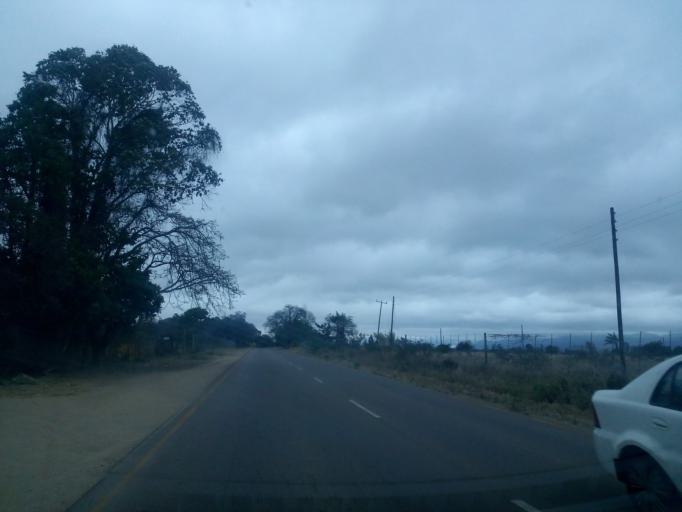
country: ZA
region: Limpopo
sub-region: Vhembe District Municipality
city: Louis Trichardt
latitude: -23.0786
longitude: 29.9057
